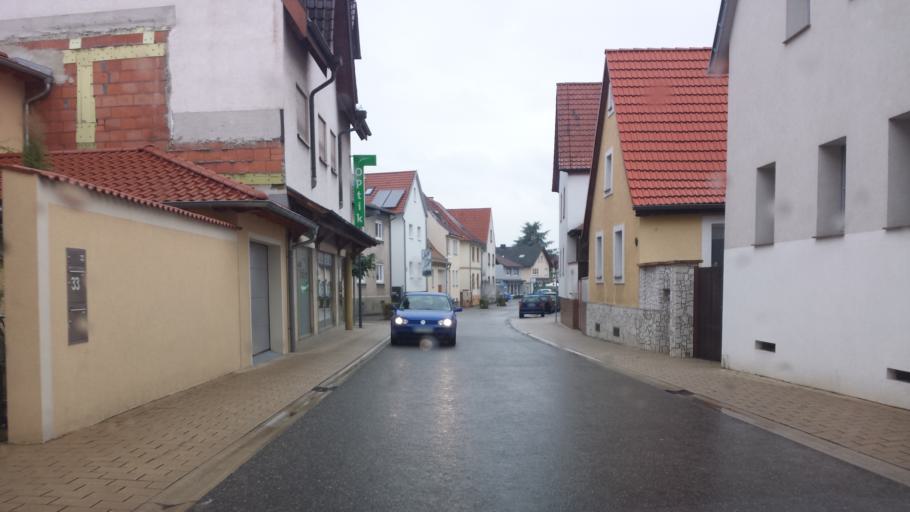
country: DE
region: Baden-Wuerttemberg
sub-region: Karlsruhe Region
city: Rauenberg
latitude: 49.2679
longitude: 8.7028
